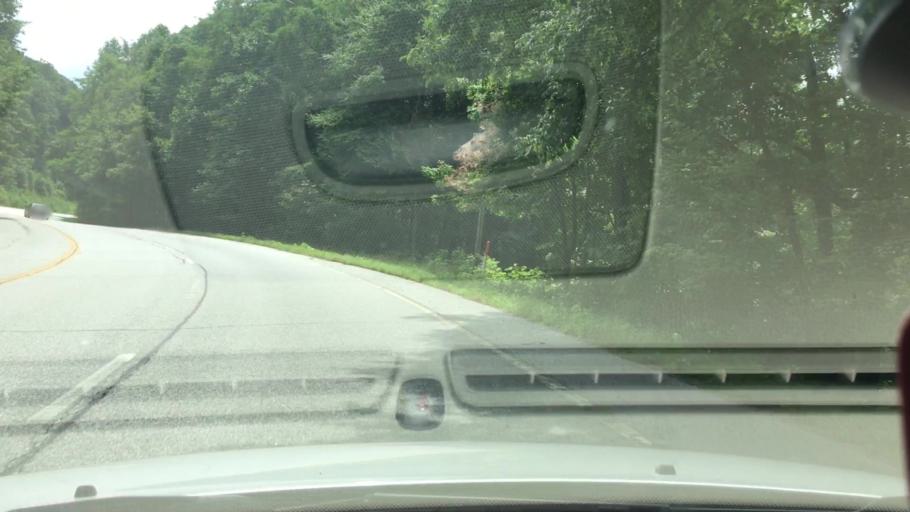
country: US
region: Georgia
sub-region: Union County
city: Blairsville
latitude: 34.7599
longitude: -83.9243
